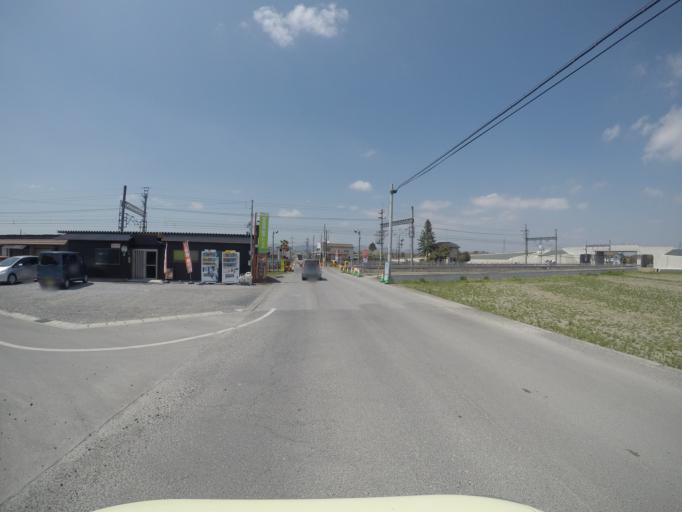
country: JP
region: Tochigi
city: Tochigi
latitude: 36.4321
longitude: 139.7481
